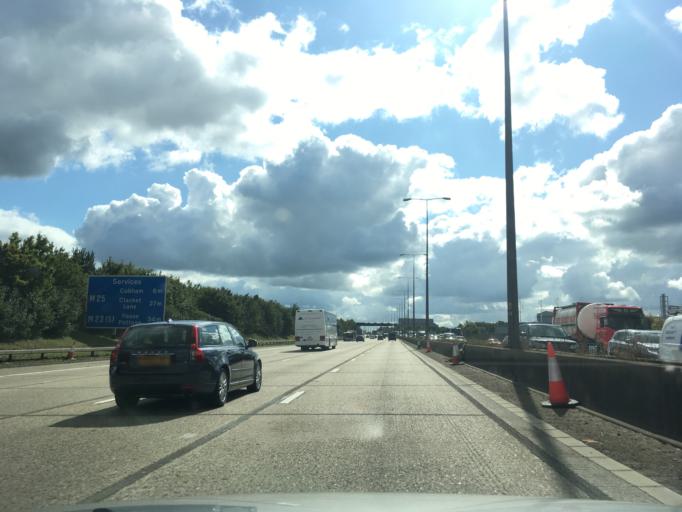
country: GB
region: England
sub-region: Surrey
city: Addlestone
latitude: 51.3577
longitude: -0.4947
